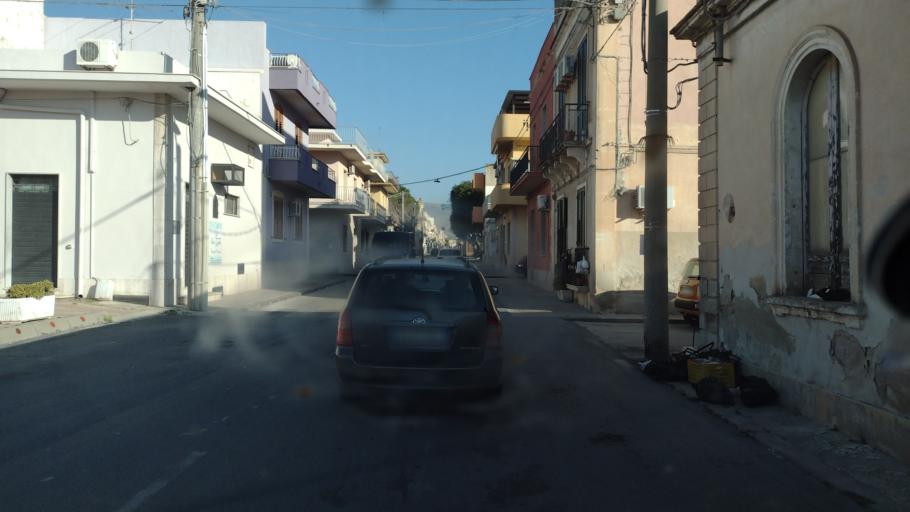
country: IT
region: Sicily
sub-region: Provincia di Siracusa
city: Avola
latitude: 36.9035
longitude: 15.1371
